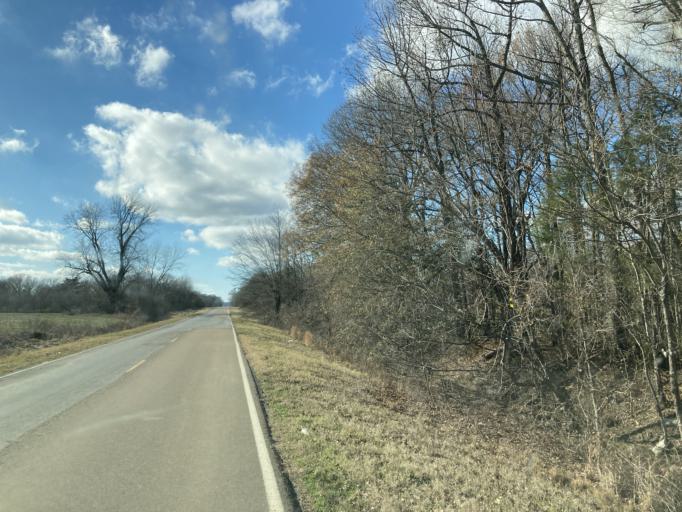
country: US
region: Mississippi
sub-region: Yazoo County
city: Yazoo City
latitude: 32.9652
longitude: -90.4649
